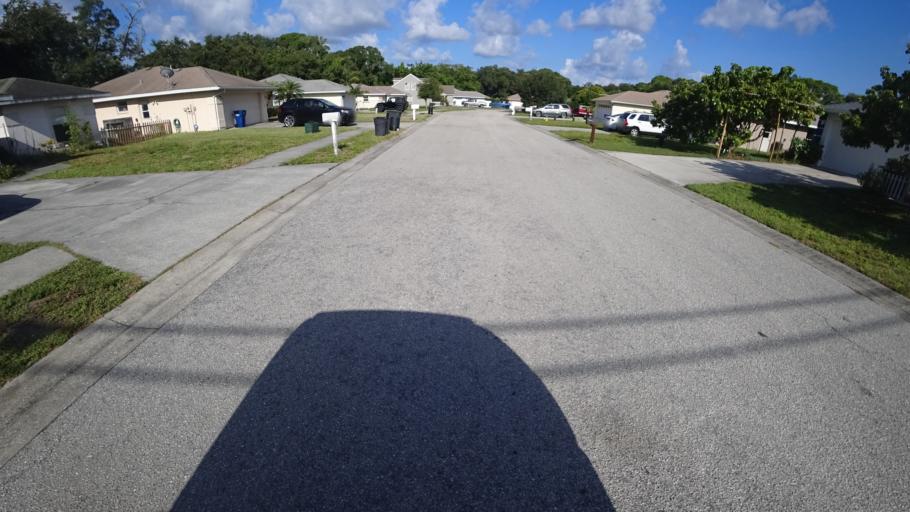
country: US
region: Florida
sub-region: Manatee County
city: South Bradenton
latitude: 27.4656
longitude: -82.5940
